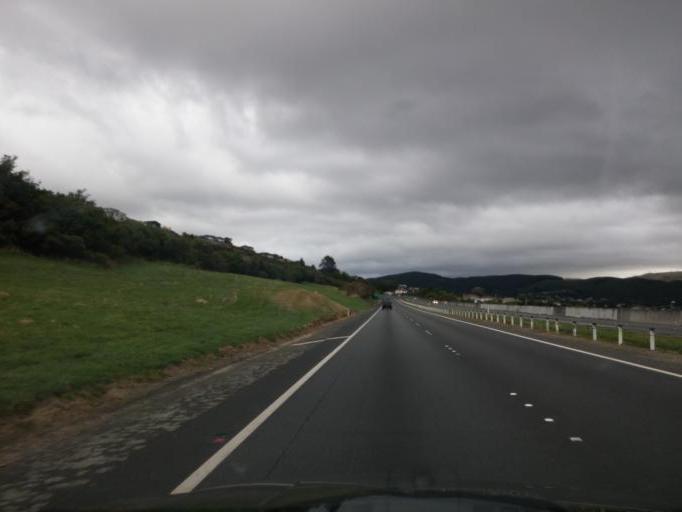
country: NZ
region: Wellington
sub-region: Porirua City
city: Porirua
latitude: -41.1645
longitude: 174.8342
